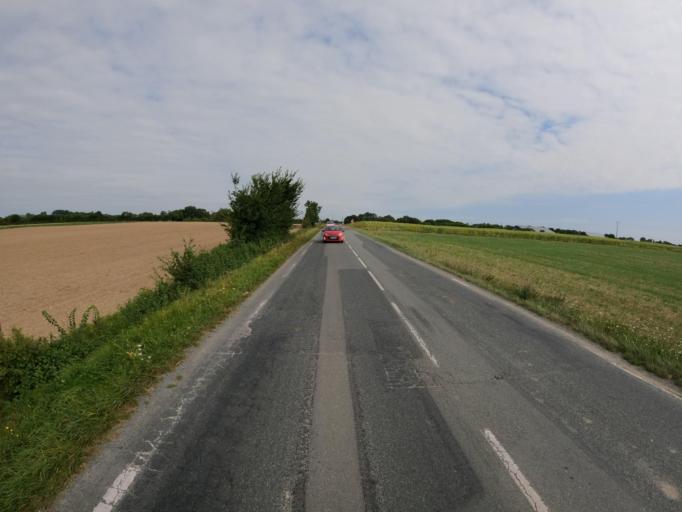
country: FR
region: Poitou-Charentes
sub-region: Departement de la Charente-Maritime
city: Saint-Jean-de-Liversay
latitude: 46.2554
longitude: -0.8815
